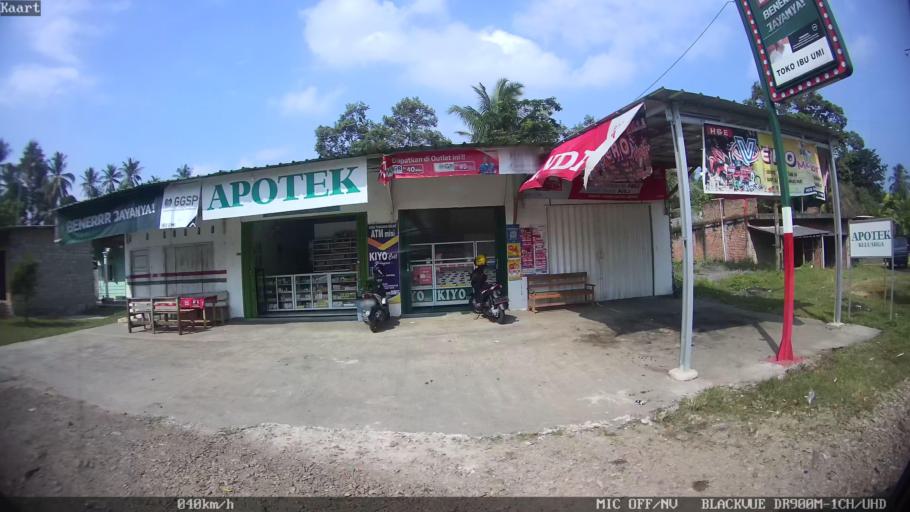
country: ID
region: Lampung
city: Natar
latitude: -5.3697
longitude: 105.1917
